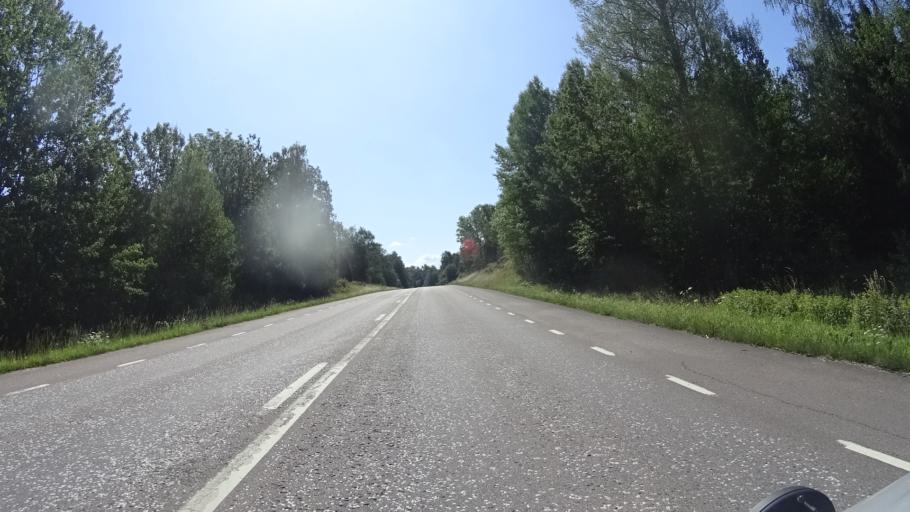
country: SE
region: OEstergoetland
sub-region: Vadstena Kommun
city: Herrestad
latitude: 58.3087
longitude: 14.9104
